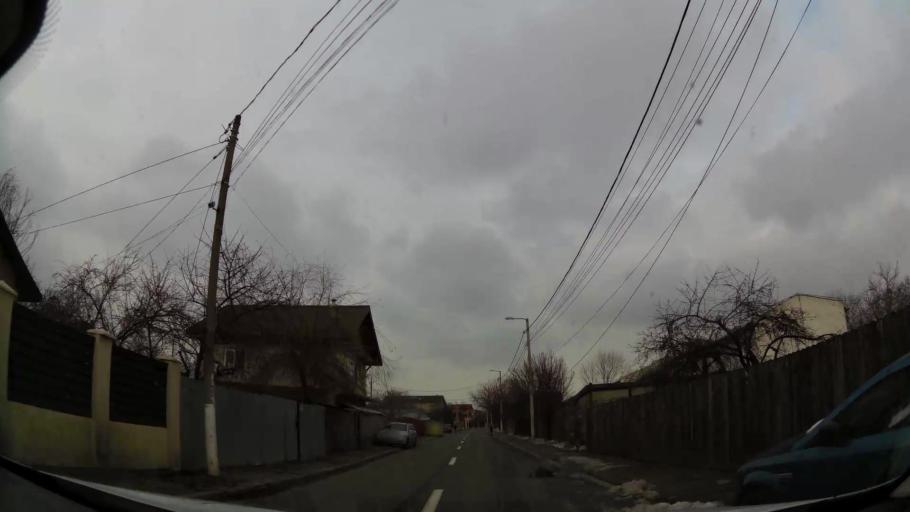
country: RO
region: Ilfov
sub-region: Voluntari City
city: Voluntari
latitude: 44.4947
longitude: 26.1667
